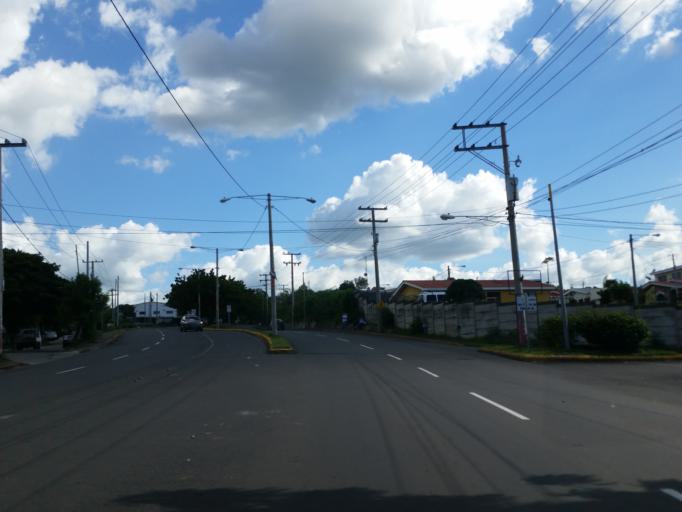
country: NI
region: Managua
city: Managua
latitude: 12.1185
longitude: -86.2839
